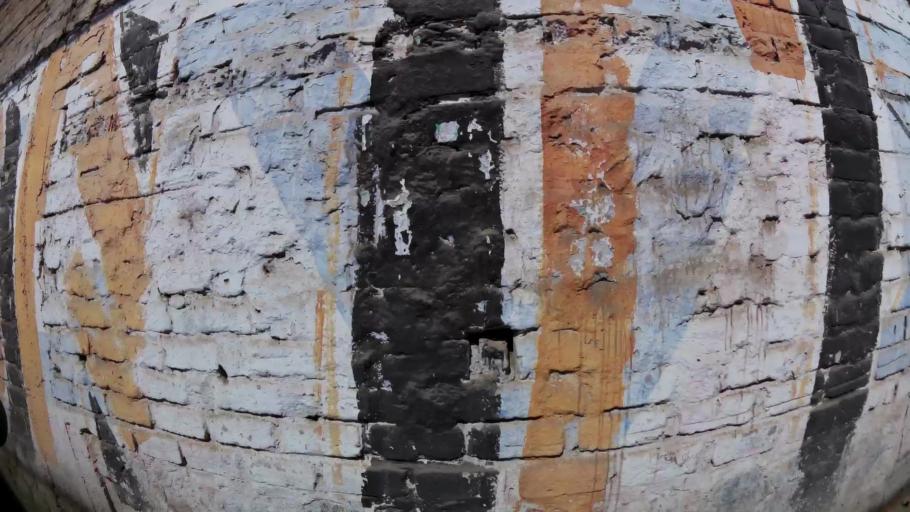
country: PE
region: Ica
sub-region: Provincia de Ica
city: Ica
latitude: -14.0611
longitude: -75.7231
